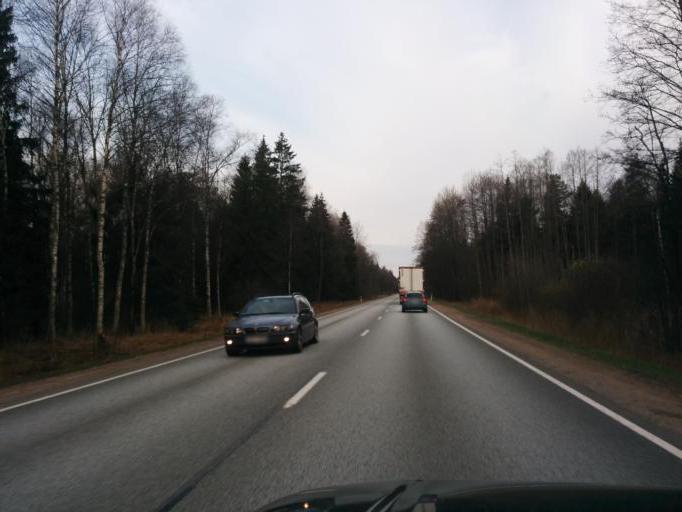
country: LV
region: Kekava
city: Balozi
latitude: 56.8194
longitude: 24.1024
